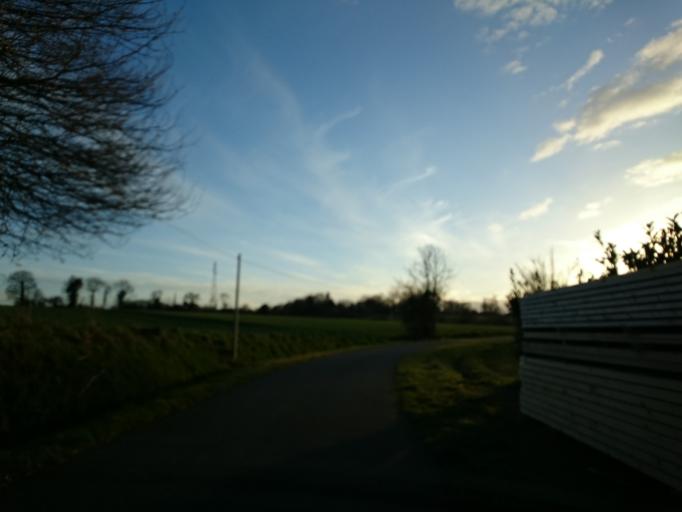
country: FR
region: Brittany
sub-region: Departement d'Ille-et-Vilaine
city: Chanteloup
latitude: 47.9182
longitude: -1.6044
